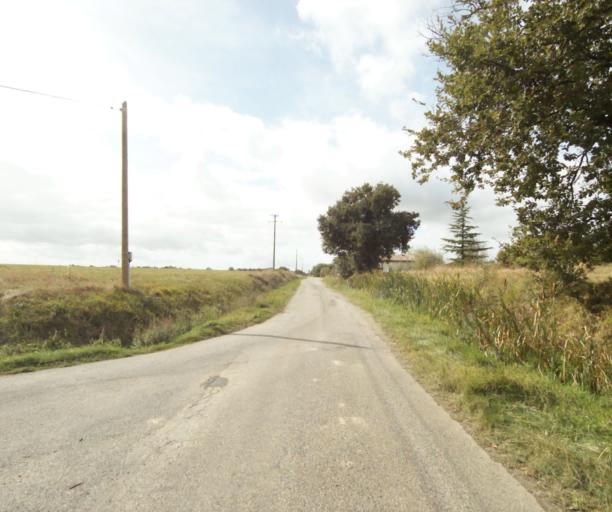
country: FR
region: Midi-Pyrenees
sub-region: Departement du Tarn-et-Garonne
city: Finhan
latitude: 43.8839
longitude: 1.1199
